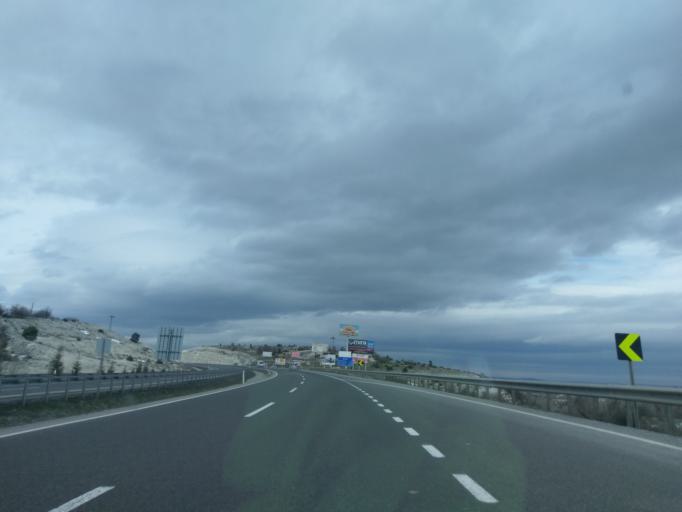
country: TR
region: Kuetahya
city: Kutahya
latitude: 39.3724
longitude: 30.0662
